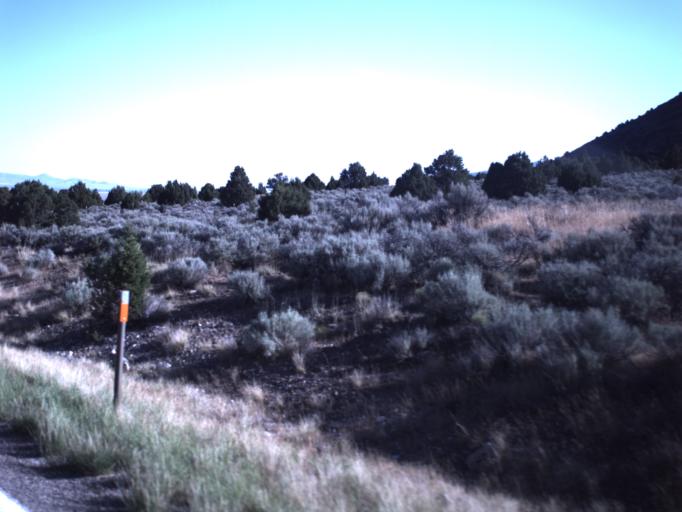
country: US
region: Utah
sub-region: Beaver County
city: Milford
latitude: 38.1260
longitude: -112.9560
